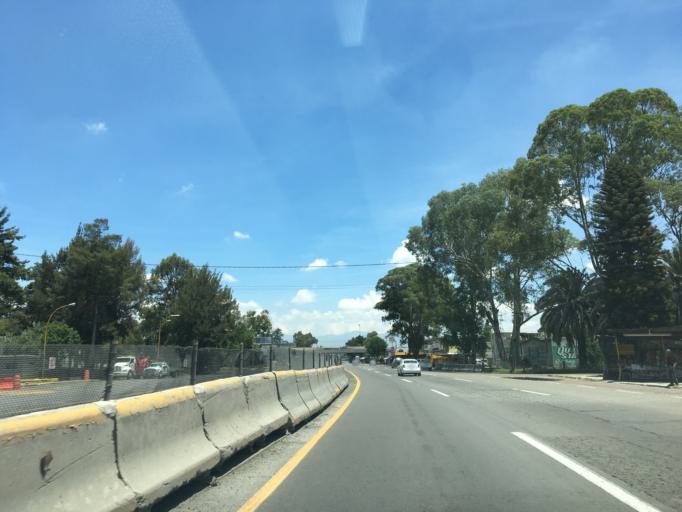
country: MX
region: Puebla
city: San Martin Texmelucan de Labastida
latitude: 19.2708
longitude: -98.4291
